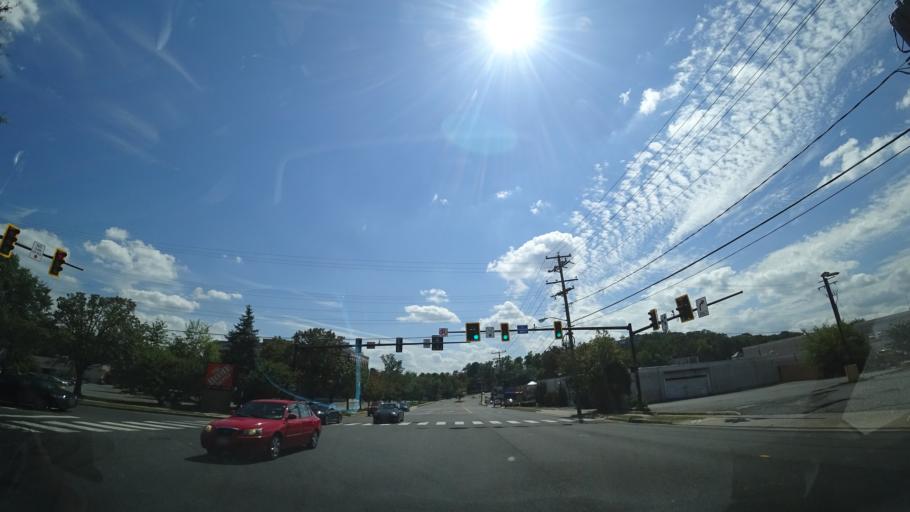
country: US
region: Virginia
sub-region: Fairfax County
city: Mantua
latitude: 38.8636
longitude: -77.2761
